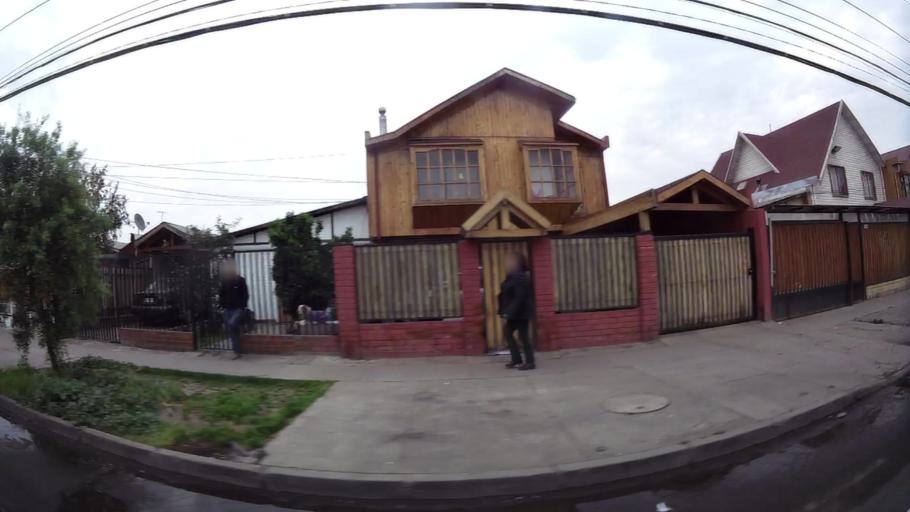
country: CL
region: Santiago Metropolitan
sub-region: Provincia de Santiago
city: Lo Prado
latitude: -33.4918
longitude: -70.7357
